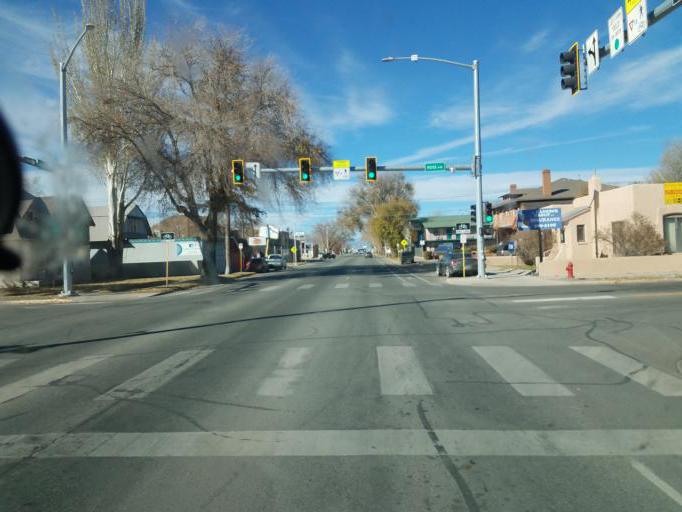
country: US
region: Colorado
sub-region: Alamosa County
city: Alamosa
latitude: 37.4682
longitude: -105.8699
